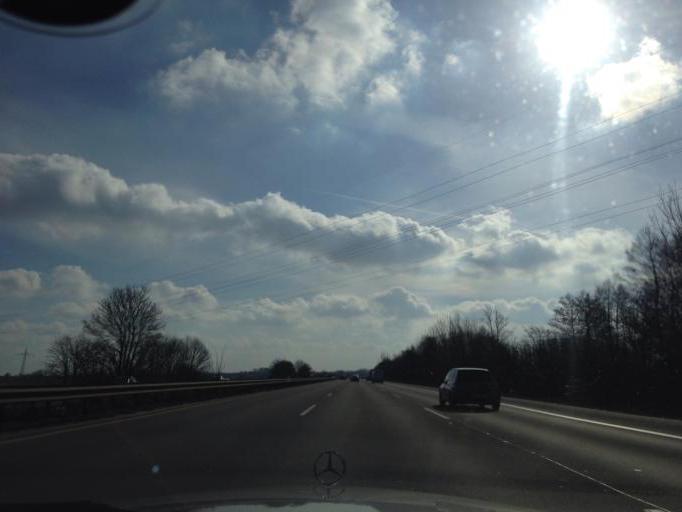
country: DE
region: Hamburg
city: Harburg
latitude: 53.4372
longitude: 10.0315
